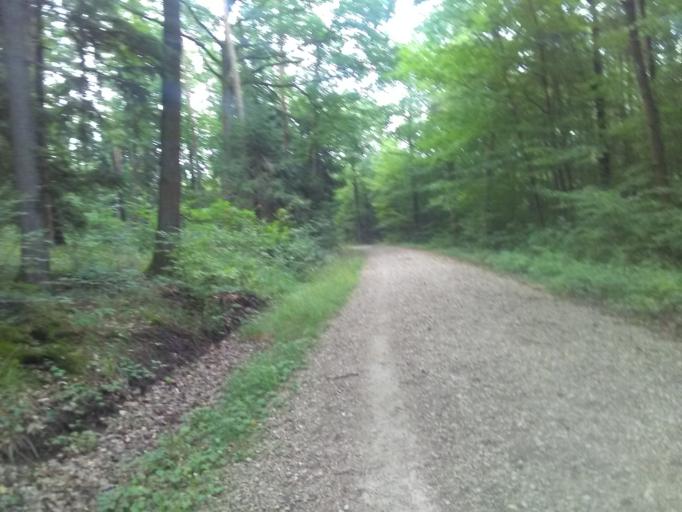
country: DE
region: Bavaria
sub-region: Upper Franconia
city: Pettstadt
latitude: 49.8523
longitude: 10.9094
